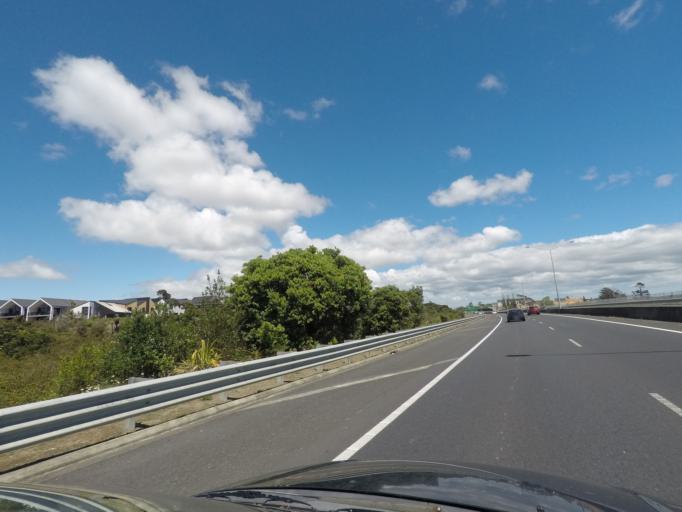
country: NZ
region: Auckland
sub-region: Auckland
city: North Shore
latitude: -36.7866
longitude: 174.6629
